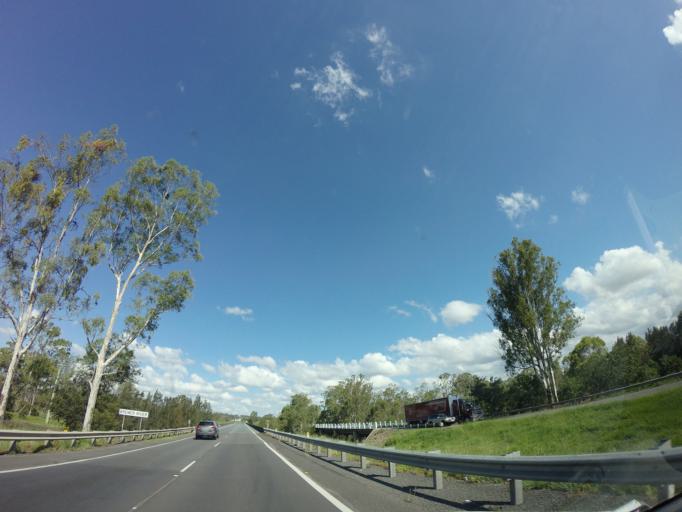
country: AU
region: Queensland
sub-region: Ipswich
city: Bundamba
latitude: -27.5822
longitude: 152.8127
